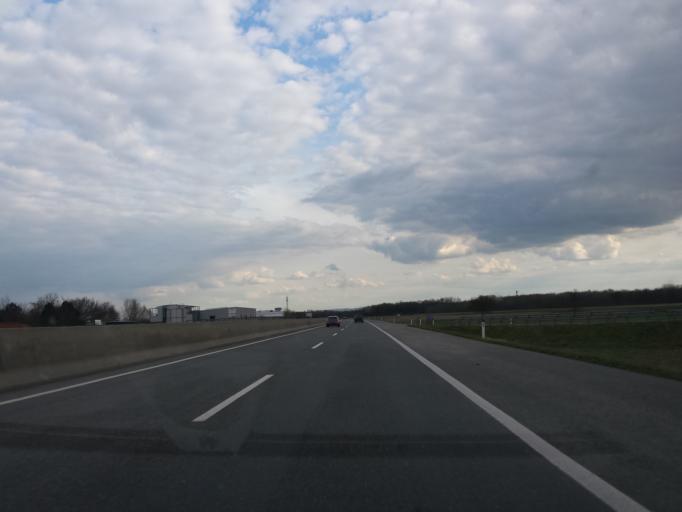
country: AT
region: Lower Austria
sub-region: Politischer Bezirk Tulln
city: Kirchberg am Wagram
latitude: 48.3916
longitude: 15.9177
